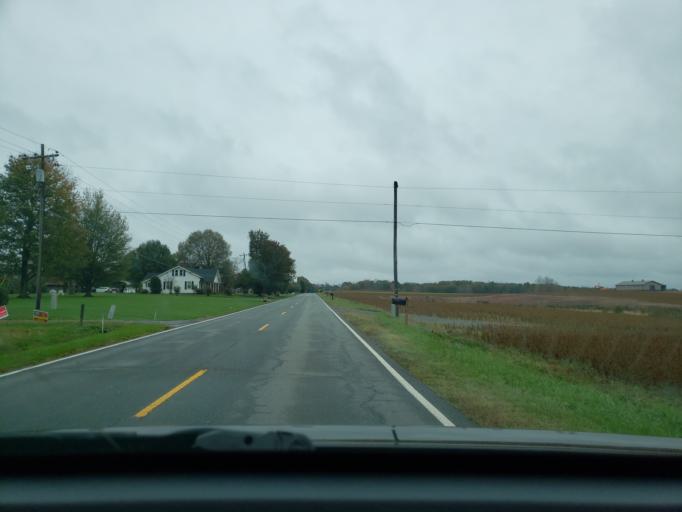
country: US
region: North Carolina
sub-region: Stokes County
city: Walnut Cove
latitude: 36.3319
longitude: -80.1481
